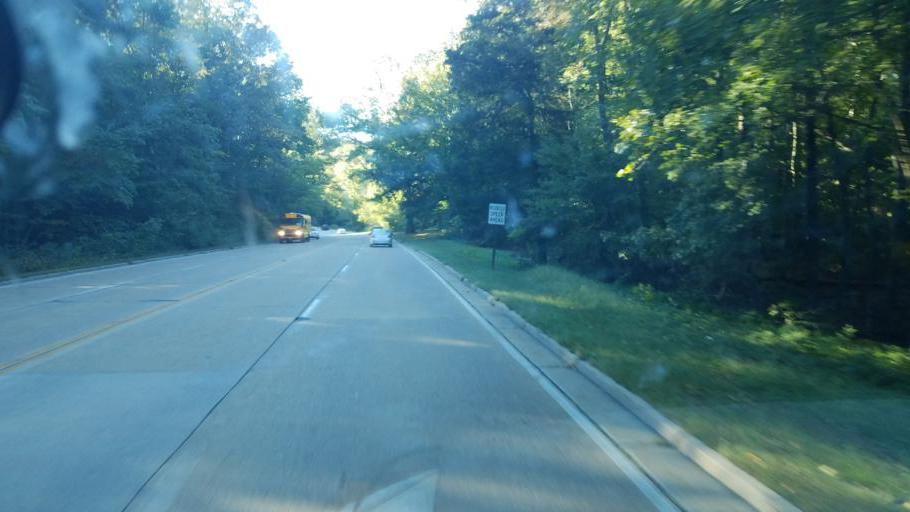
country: US
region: Virginia
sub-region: Fairfax County
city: Fort Hunt
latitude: 38.7161
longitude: -77.0783
